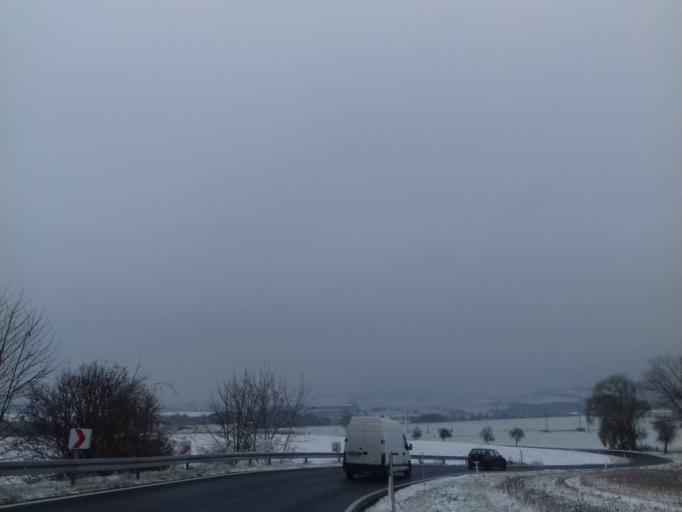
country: CZ
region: Plzensky
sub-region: Okres Domazlice
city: Domazlice
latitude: 49.4603
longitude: 12.9356
